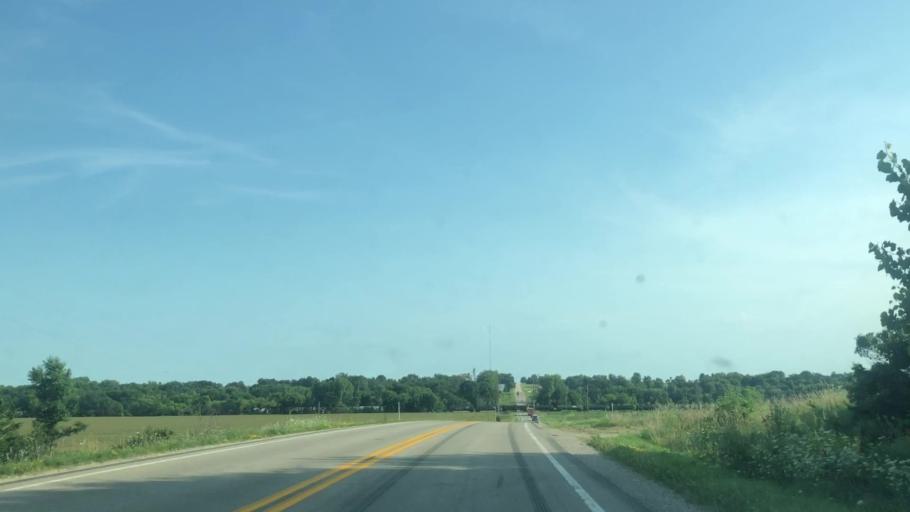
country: US
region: Iowa
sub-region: Marshall County
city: Marshalltown
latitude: 42.0346
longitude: -93.0000
